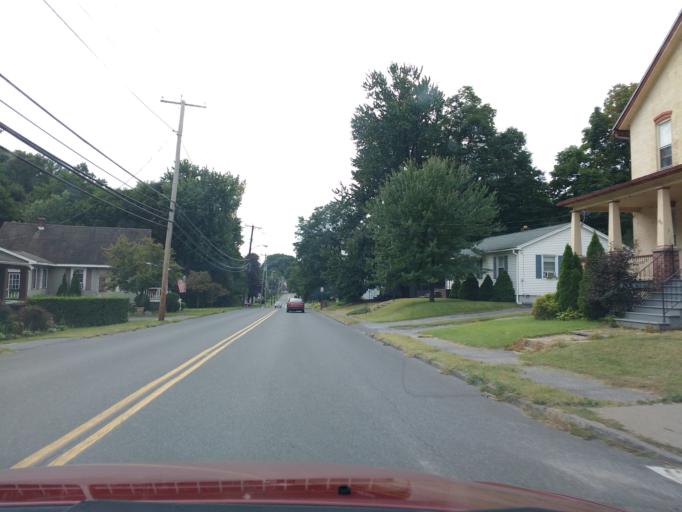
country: US
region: New York
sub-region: Ulster County
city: Kingston
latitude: 41.9334
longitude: -73.9869
